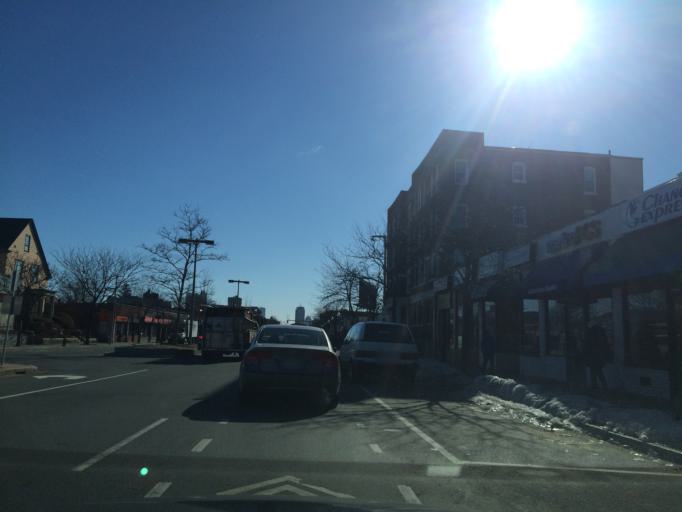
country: US
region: Massachusetts
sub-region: Norfolk County
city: Brookline
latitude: 42.3532
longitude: -71.1341
